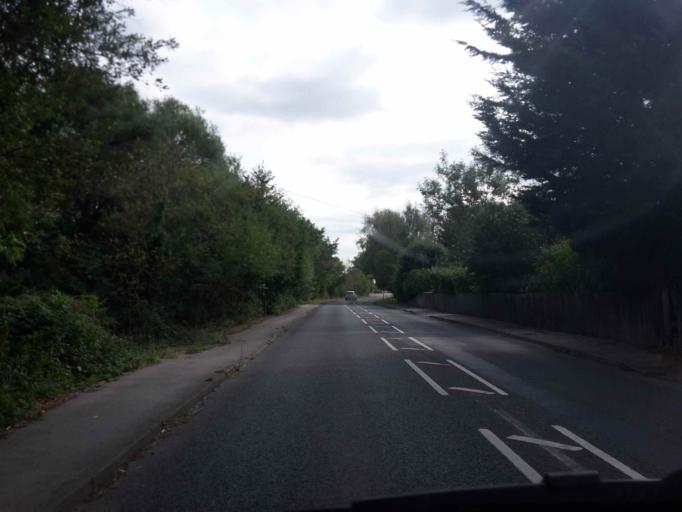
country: GB
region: England
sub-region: Wokingham
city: Twyford
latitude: 51.4660
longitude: -0.8598
